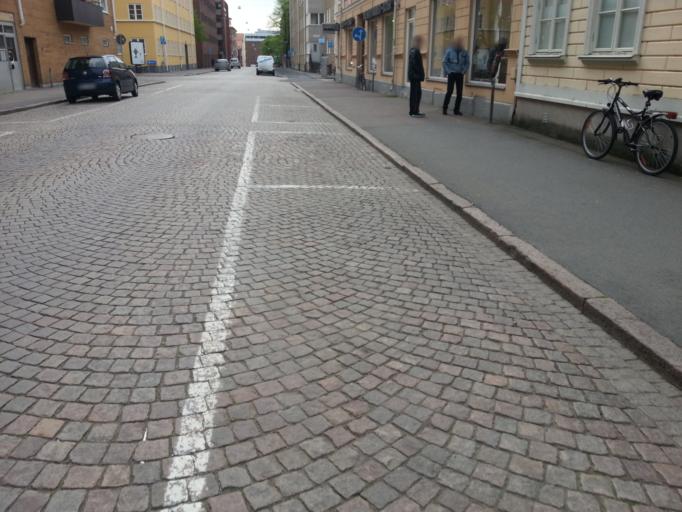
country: SE
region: Joenkoeping
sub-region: Jonkopings Kommun
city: Jonkoping
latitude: 57.7809
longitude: 14.1595
